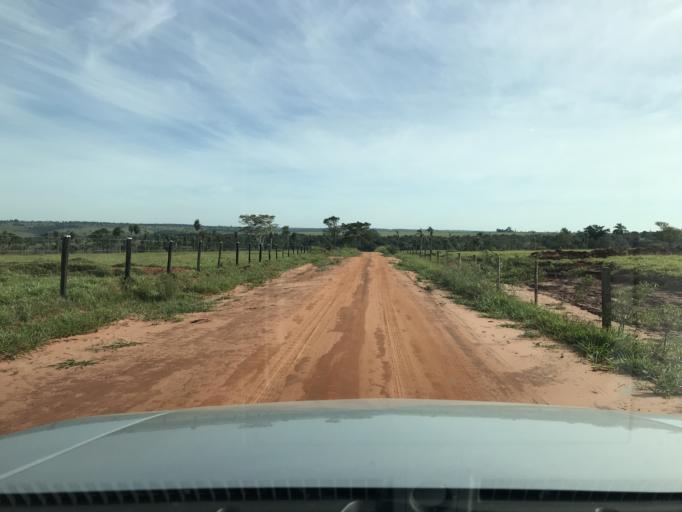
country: BR
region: Mato Grosso do Sul
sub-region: Iguatemi
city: Iguatemi
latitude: -23.6517
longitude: -54.5743
